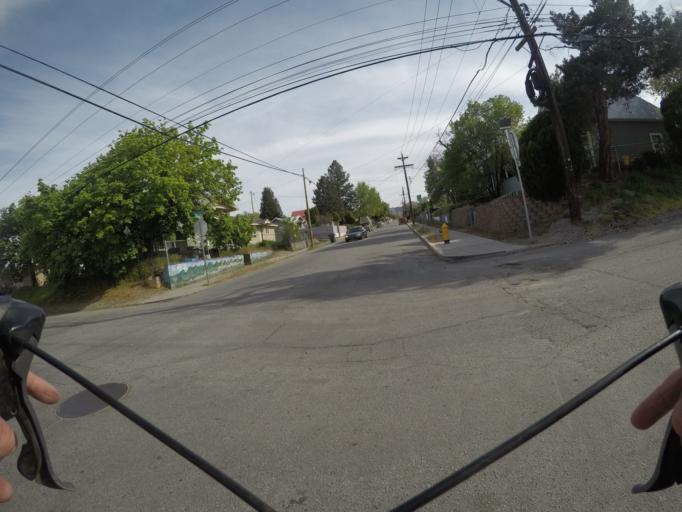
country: US
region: Washington
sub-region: Chelan County
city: Wenatchee
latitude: 47.4151
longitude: -120.3084
